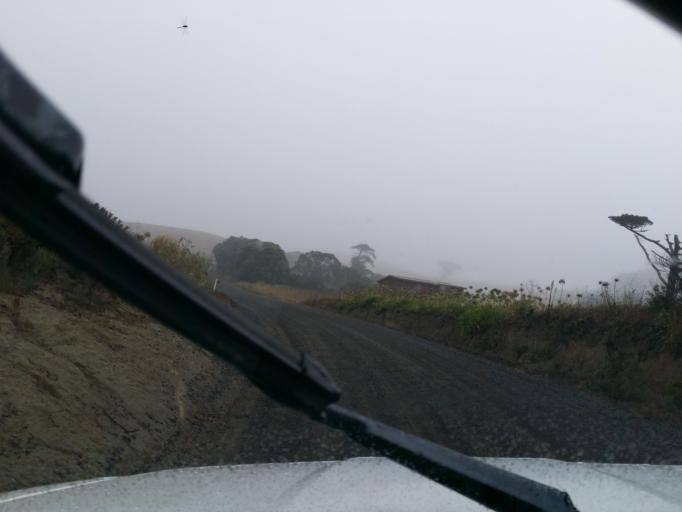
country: NZ
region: Northland
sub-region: Kaipara District
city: Dargaville
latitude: -36.0359
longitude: 173.8516
